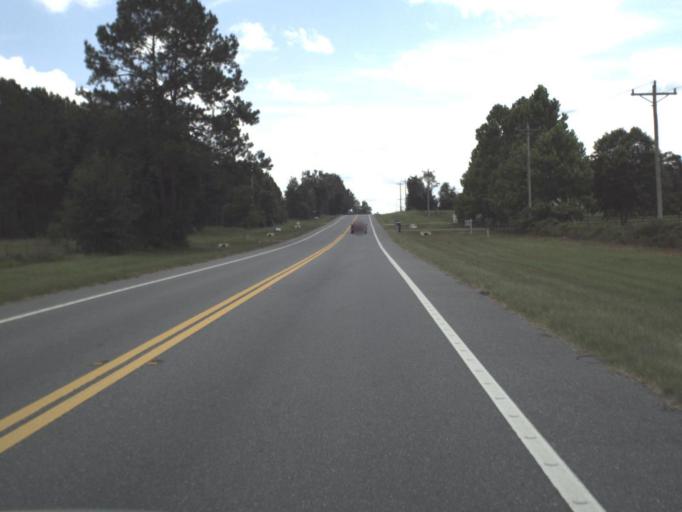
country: US
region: Florida
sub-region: Alachua County
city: High Springs
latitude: 30.0042
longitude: -82.5670
